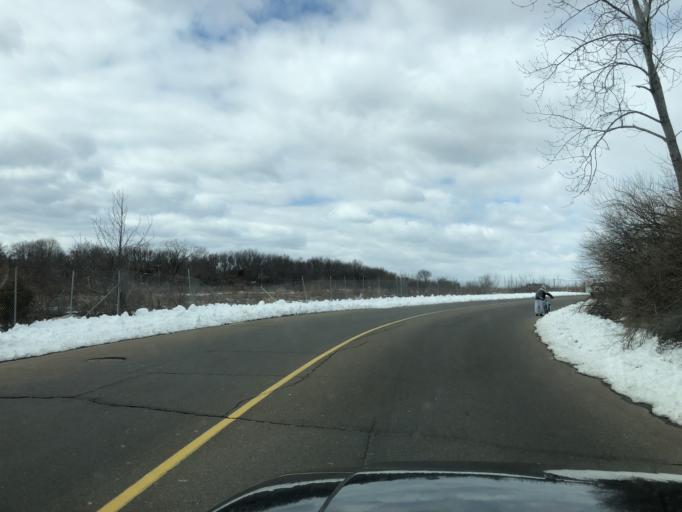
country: US
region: Connecticut
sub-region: New Haven County
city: Branford Center
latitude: 41.2780
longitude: -72.8307
